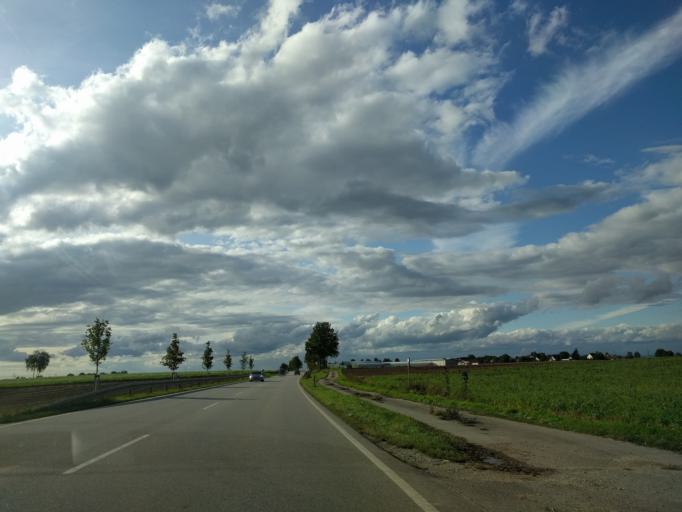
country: DE
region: Bavaria
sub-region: Lower Bavaria
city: Stephansposching
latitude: 48.7988
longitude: 12.8102
